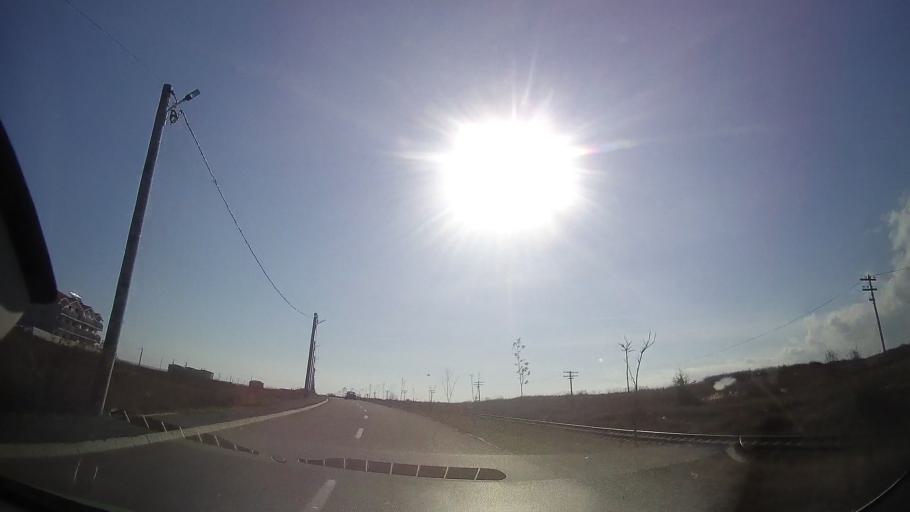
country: RO
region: Constanta
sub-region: Comuna Costinesti
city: Schitu
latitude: 43.9347
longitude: 28.6308
